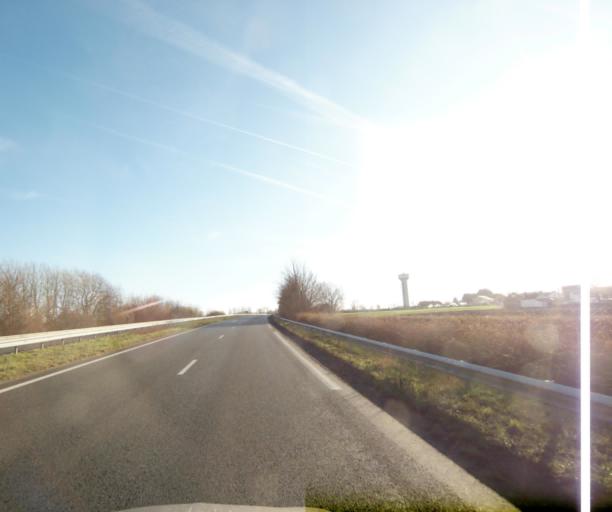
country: FR
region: Nord-Pas-de-Calais
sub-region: Departement du Nord
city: Saultain
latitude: 50.3376
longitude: 3.5876
